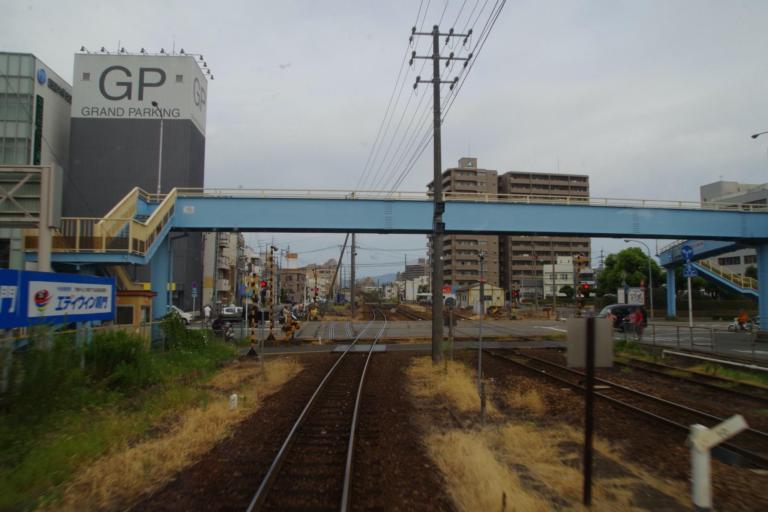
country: JP
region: Tokushima
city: Tokushima-shi
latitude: 34.0756
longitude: 134.5491
